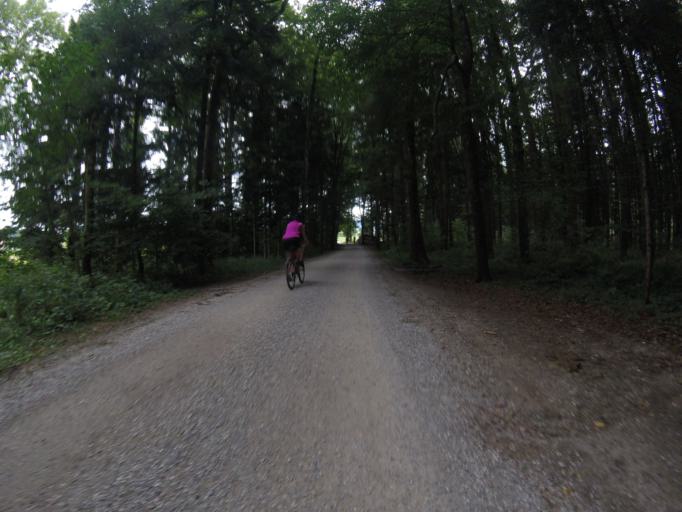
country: CH
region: Bern
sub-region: Bern-Mittelland District
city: Rubigen
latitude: 46.9104
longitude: 7.5459
